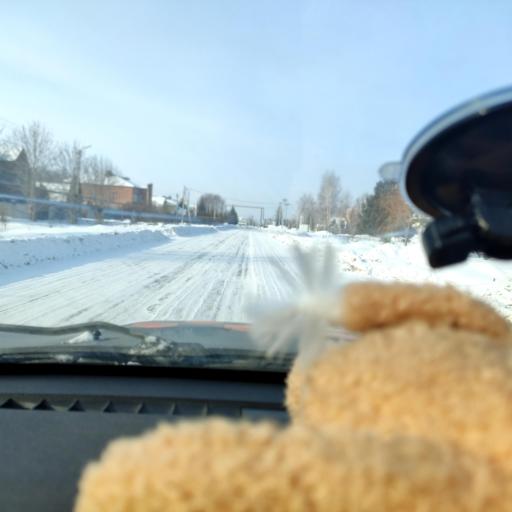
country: RU
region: Samara
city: Podstepki
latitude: 53.5106
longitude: 49.1222
